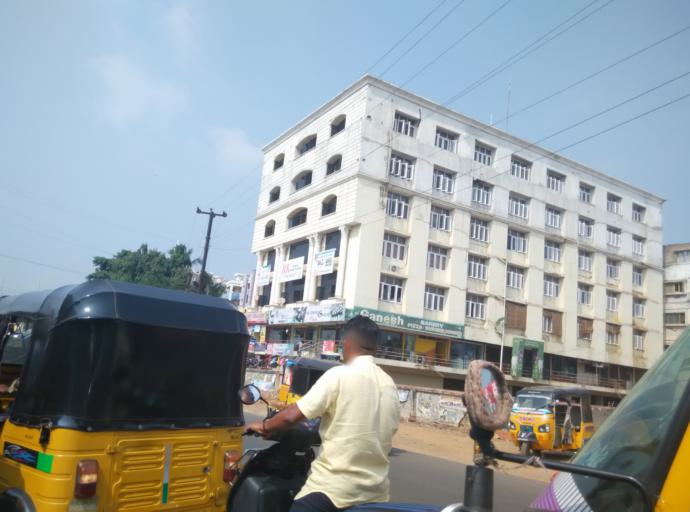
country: IN
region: Andhra Pradesh
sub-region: Vizianagaram District
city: Vizianagaram
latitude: 18.1073
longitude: 83.3973
